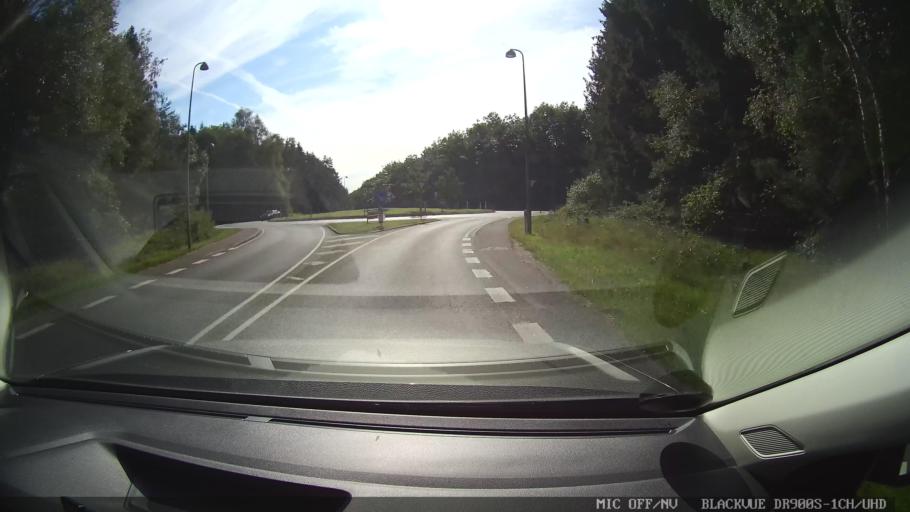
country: DK
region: North Denmark
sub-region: Mariagerfjord Kommune
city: Hadsund
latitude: 56.7246
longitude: 10.0937
